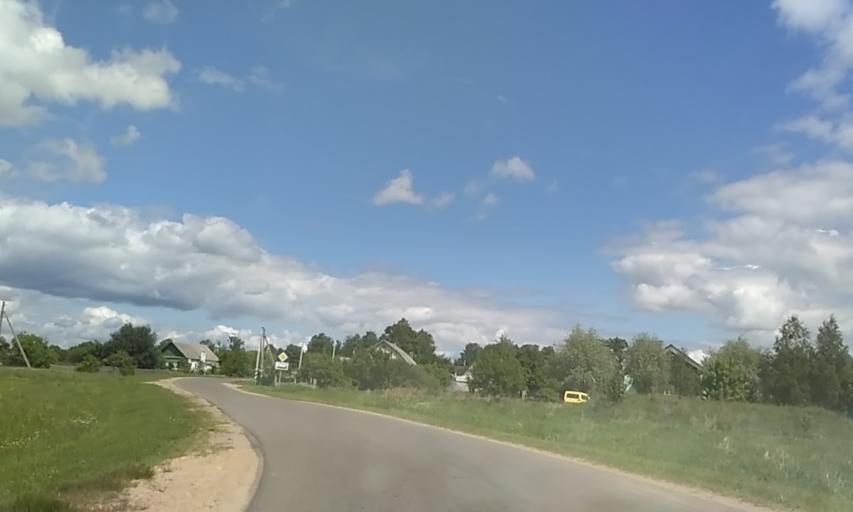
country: BY
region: Minsk
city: Krupki
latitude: 54.3617
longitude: 29.1028
